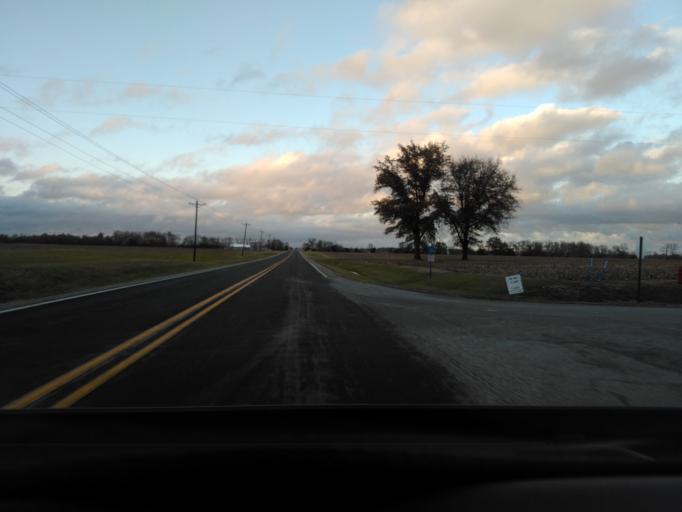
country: US
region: Illinois
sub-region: Effingham County
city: Altamont
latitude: 38.9863
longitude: -88.7488
